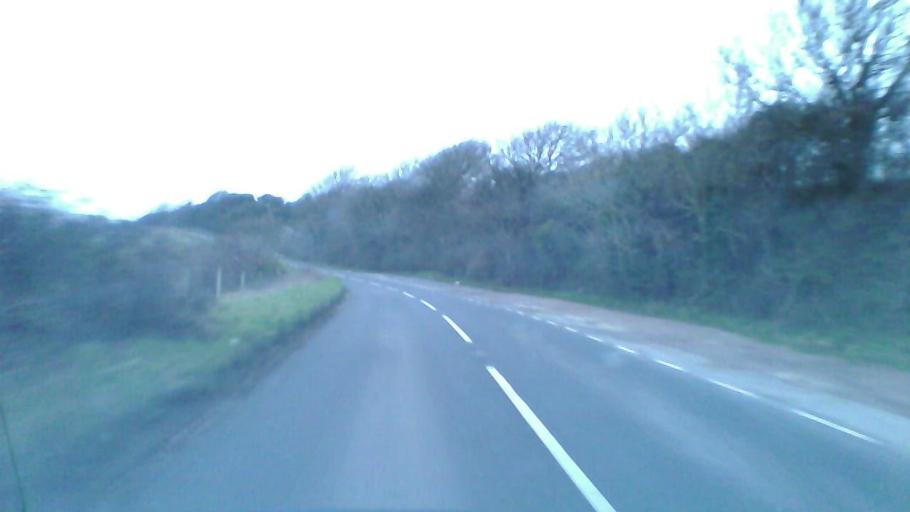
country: GB
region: England
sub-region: Isle of Wight
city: Newchurch
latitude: 50.6832
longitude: -1.1868
